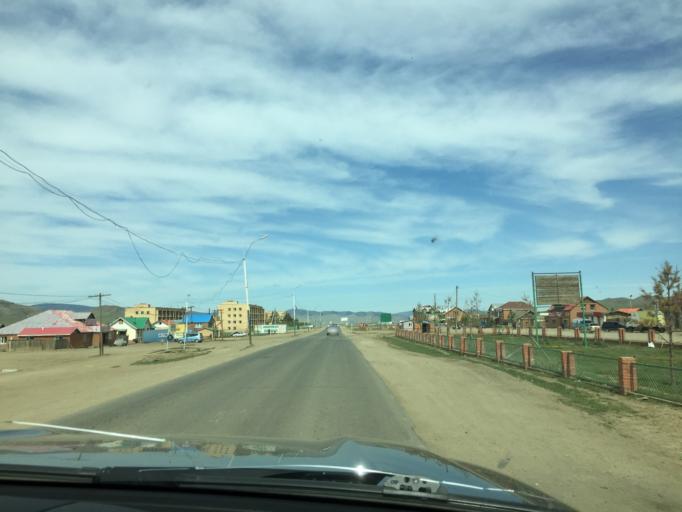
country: MN
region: Central Aimak
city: Ihsueuej
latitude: 48.2241
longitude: 106.2938
